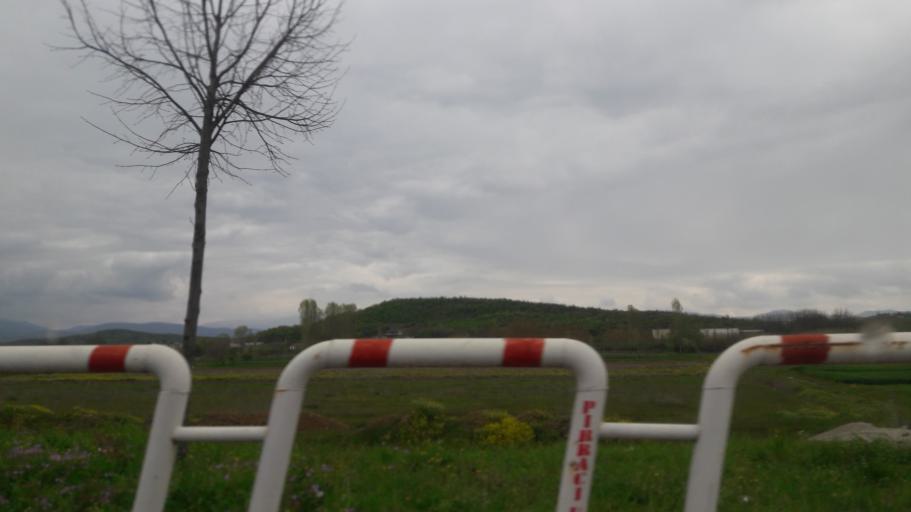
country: AL
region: Shkoder
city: Vukatane
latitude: 41.9626
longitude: 19.5372
